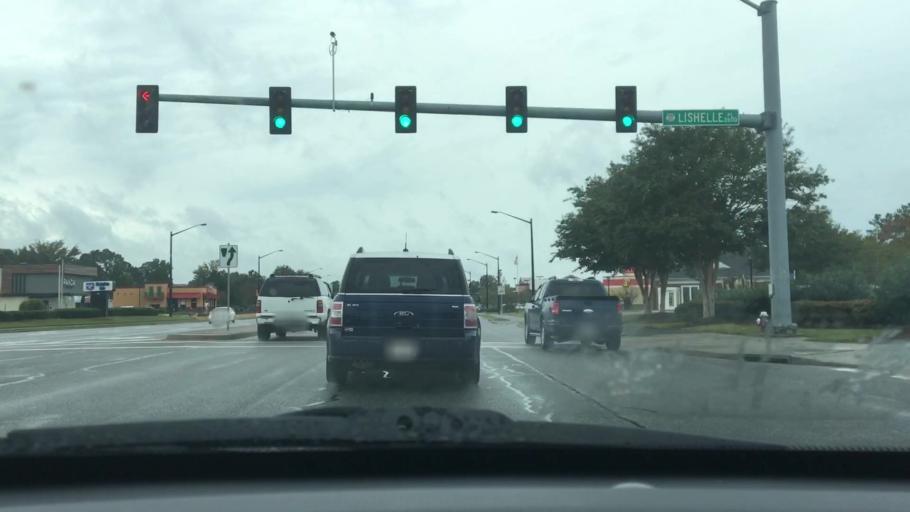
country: US
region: Virginia
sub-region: City of Virginia Beach
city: Virginia Beach
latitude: 36.8129
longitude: -76.0690
